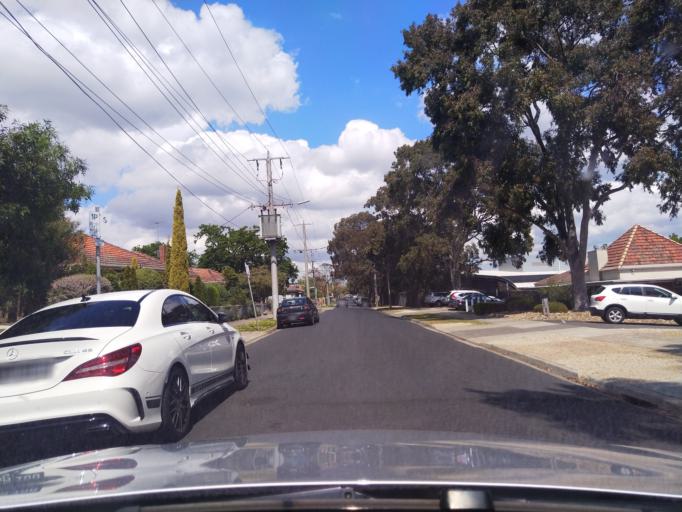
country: AU
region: Victoria
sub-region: Banyule
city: Bellfield
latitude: -37.7535
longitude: 145.0502
